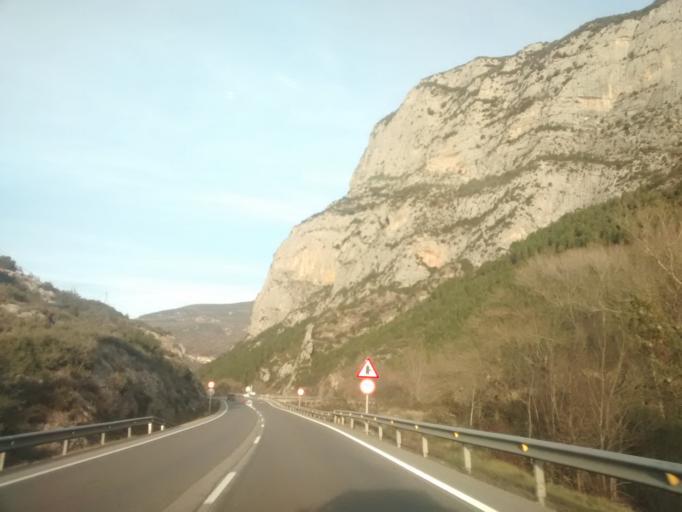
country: ES
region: Catalonia
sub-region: Provincia de Lleida
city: Coll de Nargo
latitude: 42.1849
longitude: 1.3290
